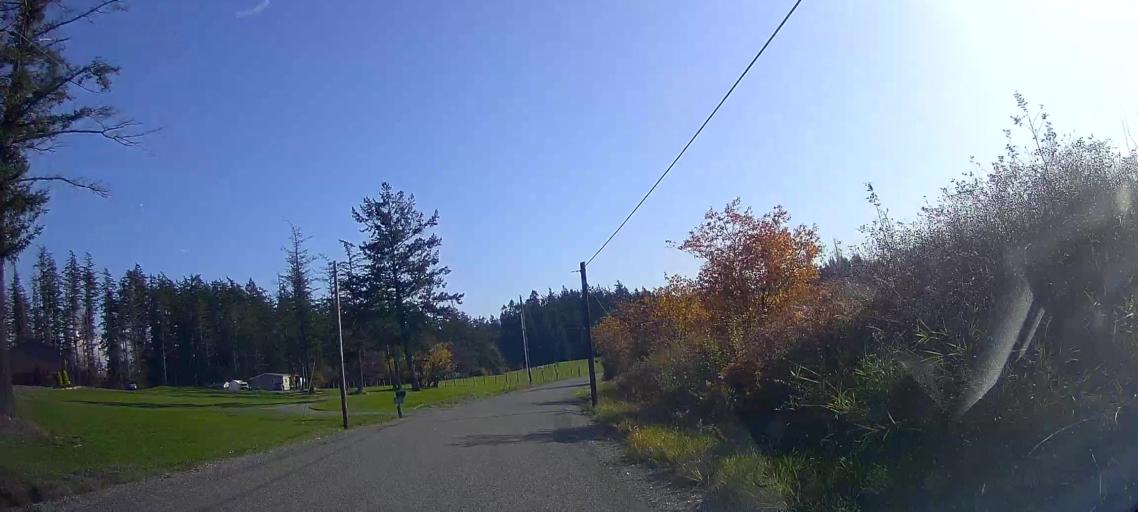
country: US
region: Washington
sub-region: Skagit County
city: Mount Vernon
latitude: 48.3692
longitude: -122.4453
